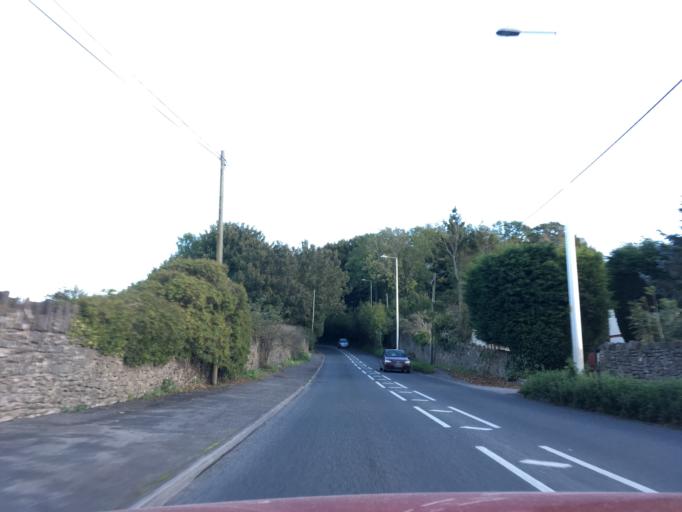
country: GB
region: England
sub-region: North Somerset
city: Long Ashton
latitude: 51.4594
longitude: -2.6593
